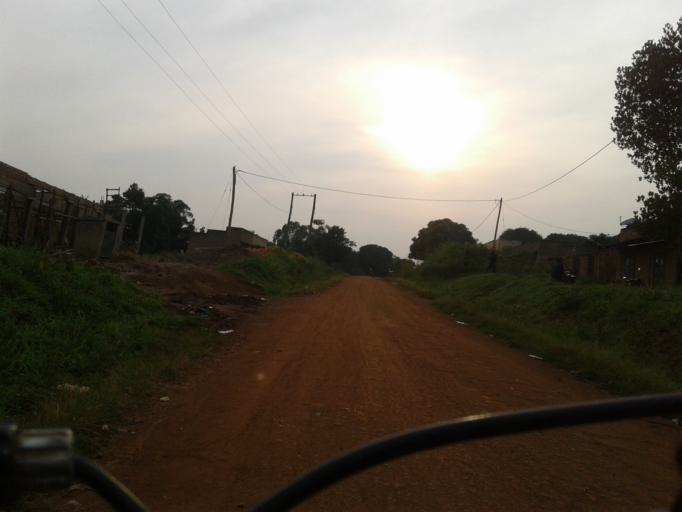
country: UG
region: Western Region
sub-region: Hoima District
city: Hoima
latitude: 1.4240
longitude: 31.3240
